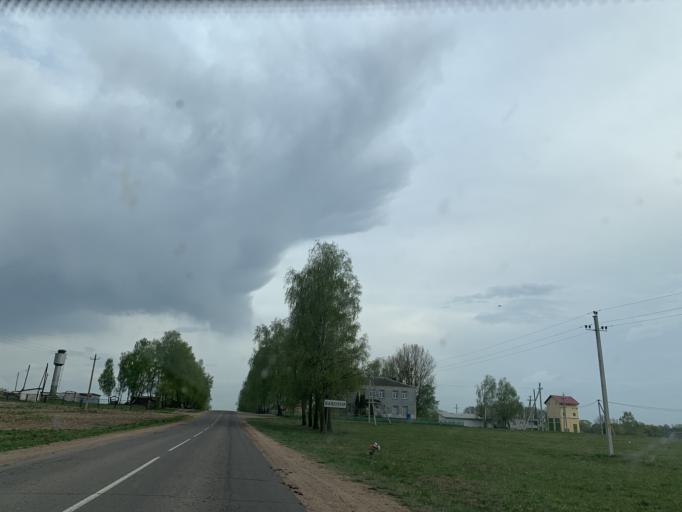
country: BY
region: Minsk
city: Kapyl'
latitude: 53.2648
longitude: 26.9572
